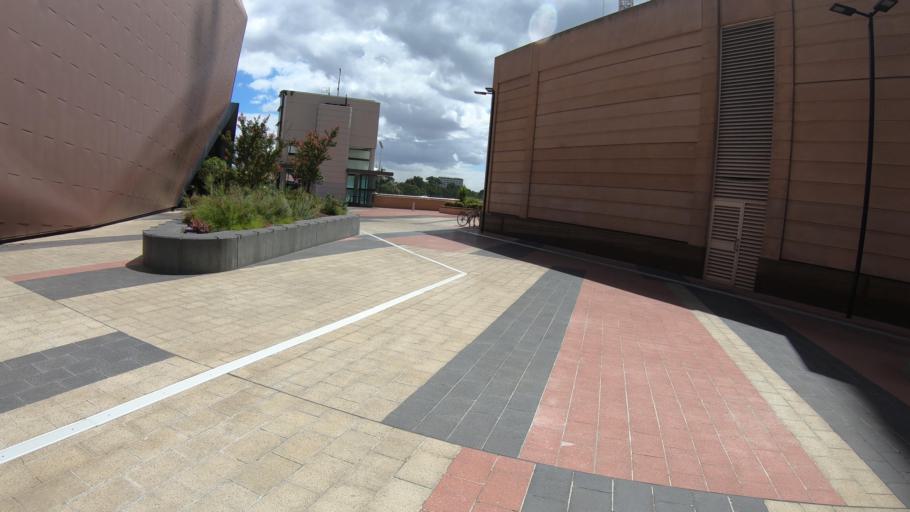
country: AU
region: South Australia
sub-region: Adelaide
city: Adelaide
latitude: -34.9206
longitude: 138.5962
